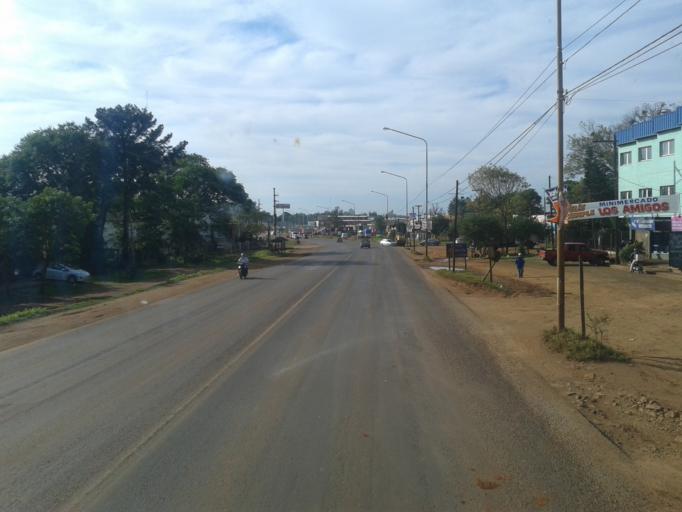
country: AR
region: Misiones
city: Garupa
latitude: -27.4368
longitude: -55.8837
